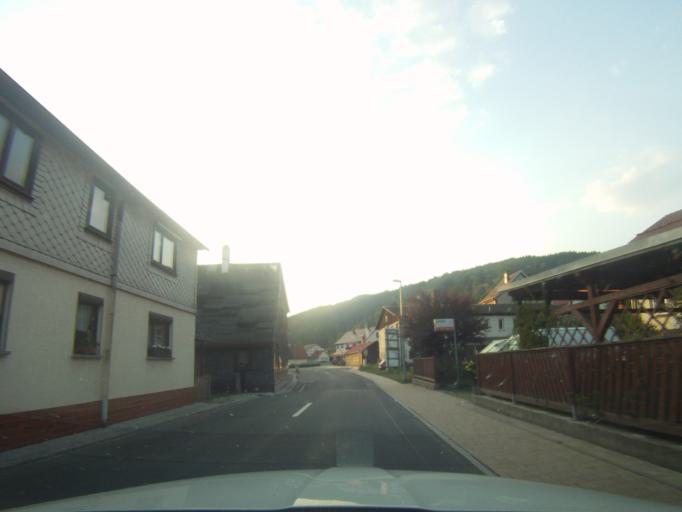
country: DE
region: Thuringia
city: Eisfeld
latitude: 50.4924
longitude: 10.8647
